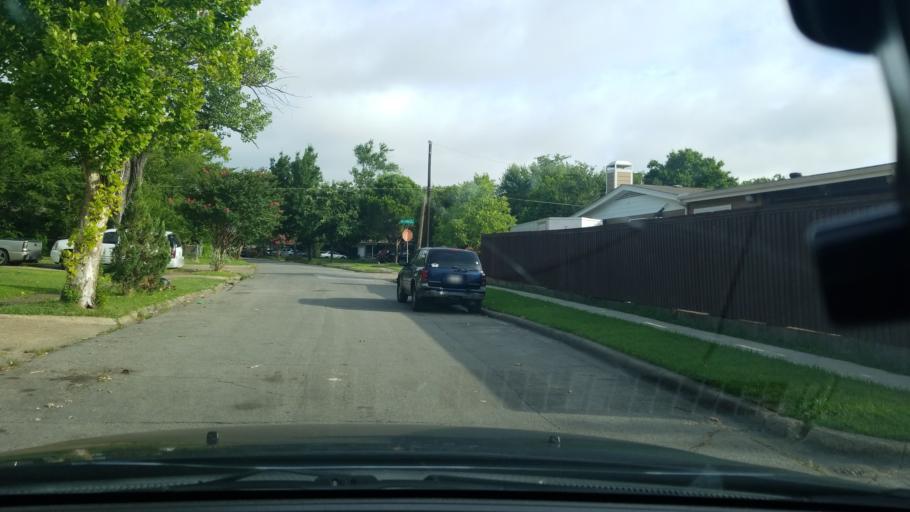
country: US
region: Texas
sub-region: Dallas County
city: Mesquite
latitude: 32.8239
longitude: -96.6601
